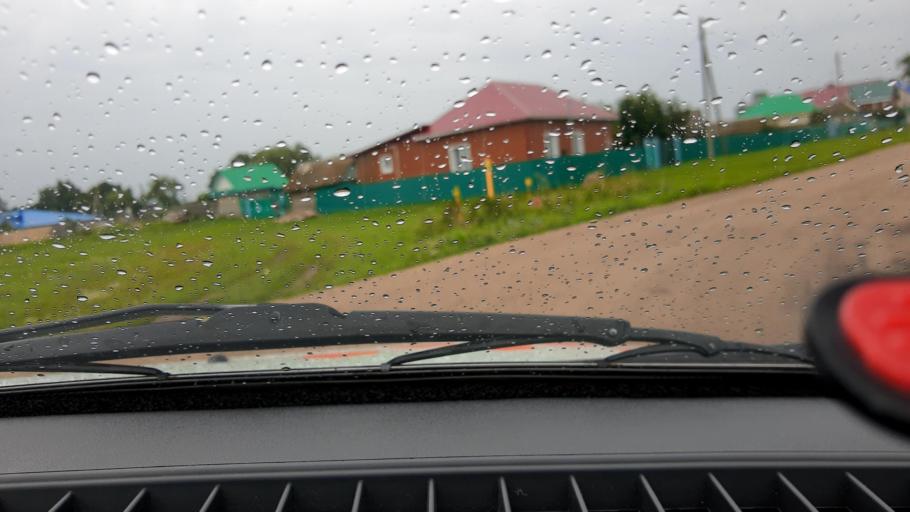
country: RU
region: Bashkortostan
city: Karmaskaly
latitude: 54.3811
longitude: 56.1144
